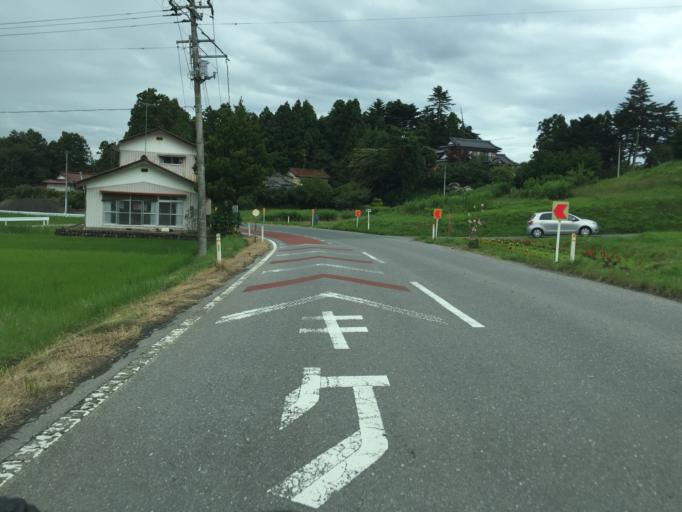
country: JP
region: Fukushima
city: Namie
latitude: 37.7481
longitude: 141.0013
